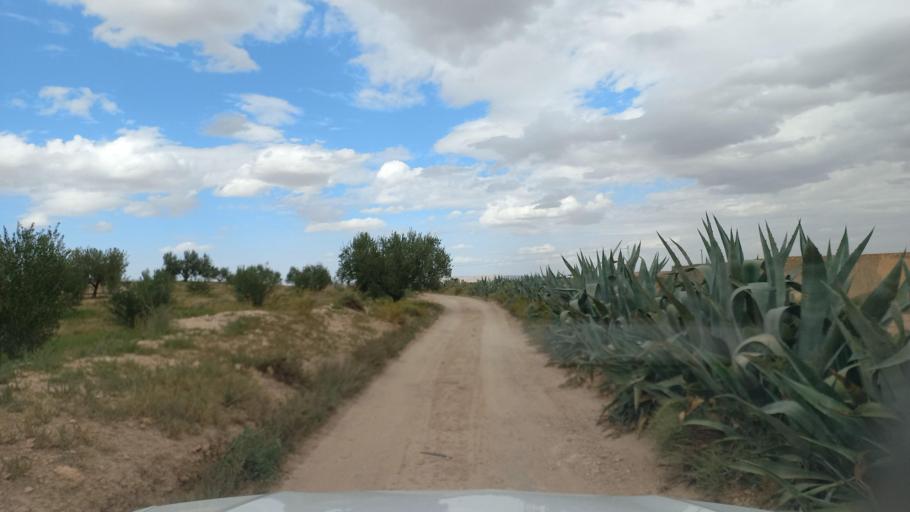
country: TN
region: Al Qasrayn
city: Sbiba
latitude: 35.4387
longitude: 9.0995
